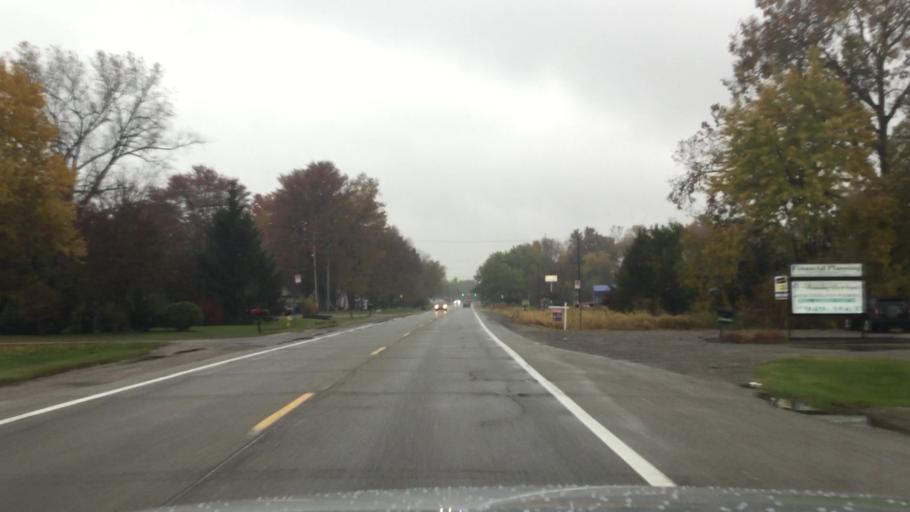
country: US
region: Michigan
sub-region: Macomb County
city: New Baltimore
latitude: 42.6513
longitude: -82.8054
